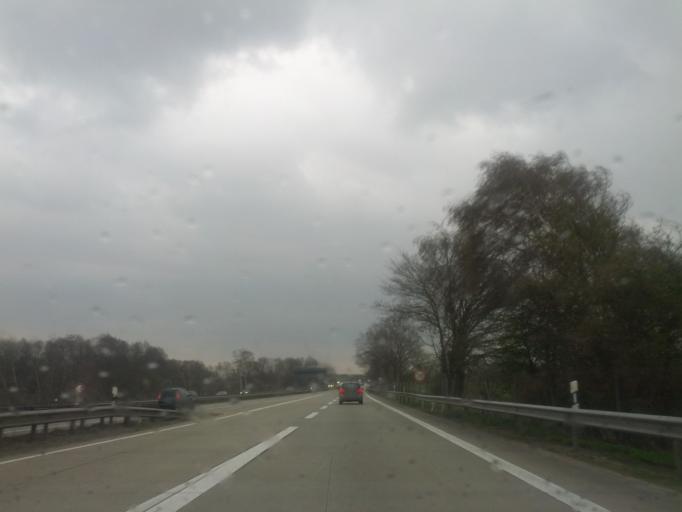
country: DE
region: Lower Saxony
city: Oyten
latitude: 53.0390
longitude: 8.9874
